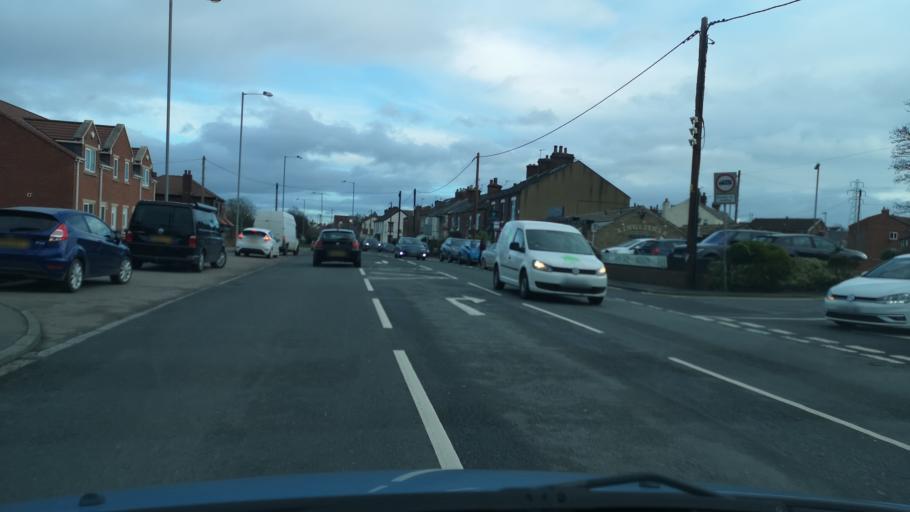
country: GB
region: England
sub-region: City and Borough of Wakefield
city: Crigglestone
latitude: 53.6472
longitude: -1.5399
